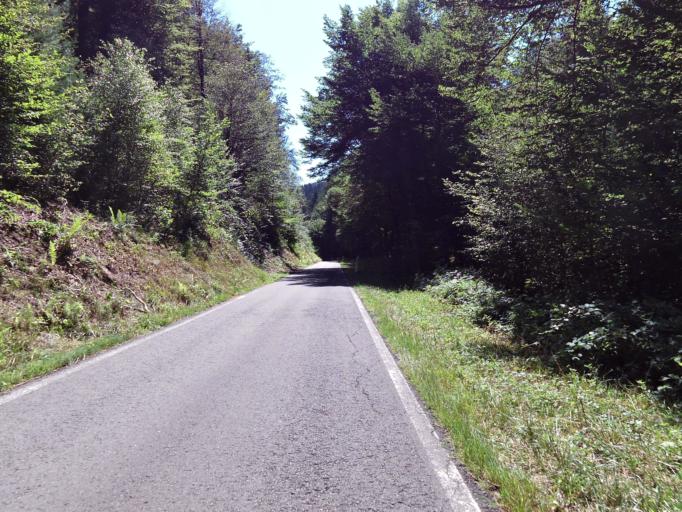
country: DE
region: Rheinland-Pfalz
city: Elmstein
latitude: 49.3850
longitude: 7.9183
